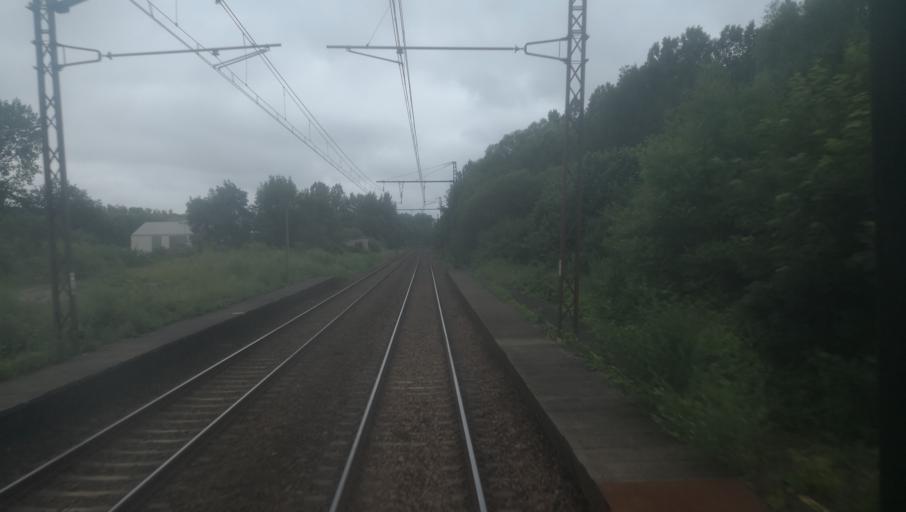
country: FR
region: Centre
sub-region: Departement de l'Indre
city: Reuilly
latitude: 47.1225
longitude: 2.0485
